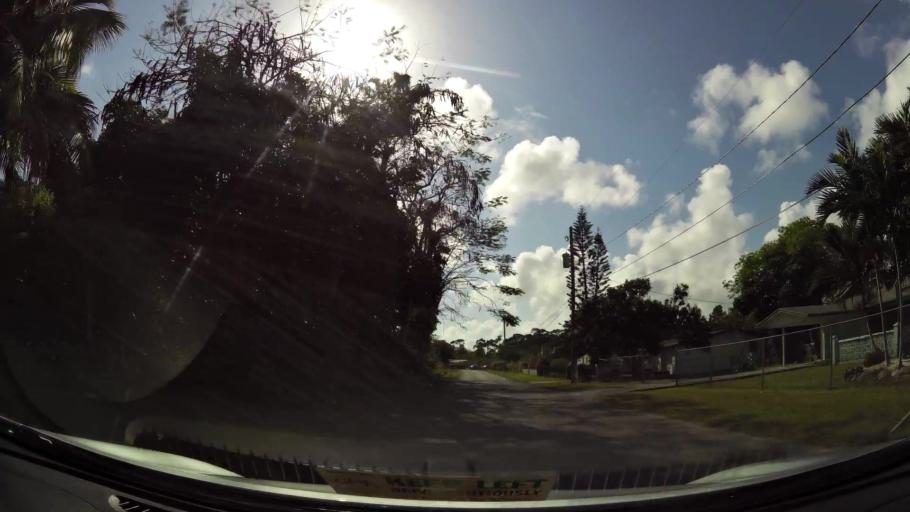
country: BS
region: Freeport
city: Lucaya
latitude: 26.5234
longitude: -78.6830
